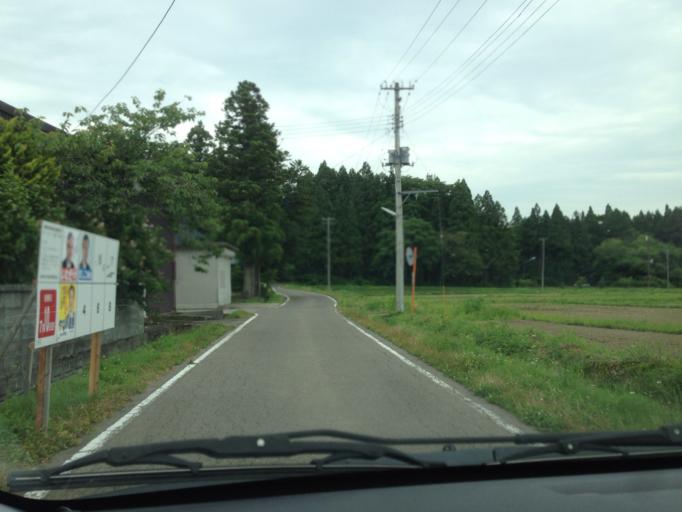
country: JP
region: Fukushima
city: Inawashiro
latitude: 37.5158
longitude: 139.9959
